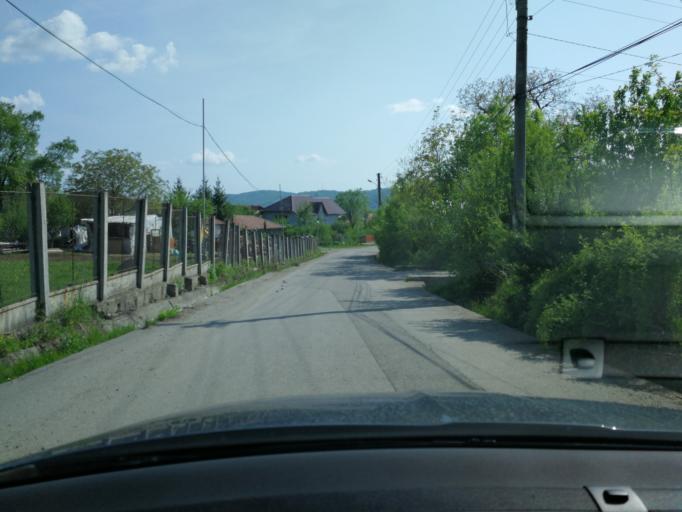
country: RO
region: Prahova
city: Cornu de Sus
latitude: 45.1656
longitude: 25.7047
